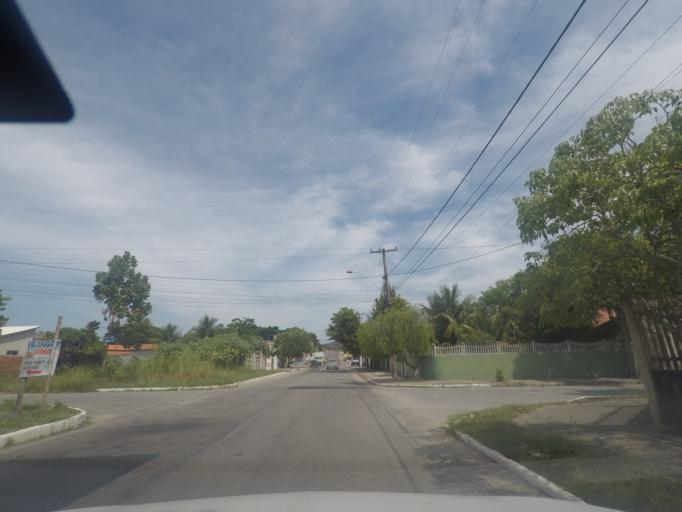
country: BR
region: Rio de Janeiro
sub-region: Marica
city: Marica
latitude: -22.9507
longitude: -42.7495
